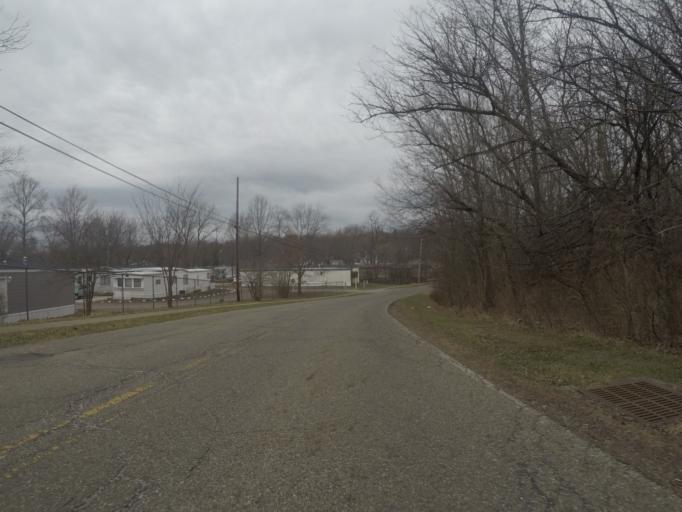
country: US
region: Ohio
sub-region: Portage County
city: Ravenna
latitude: 41.1634
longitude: -81.2647
